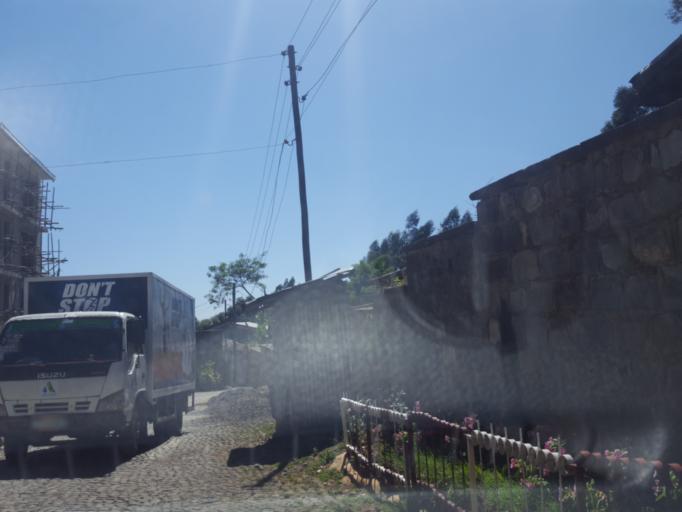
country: ET
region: Adis Abeba
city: Addis Ababa
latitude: 9.0566
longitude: 38.7450
